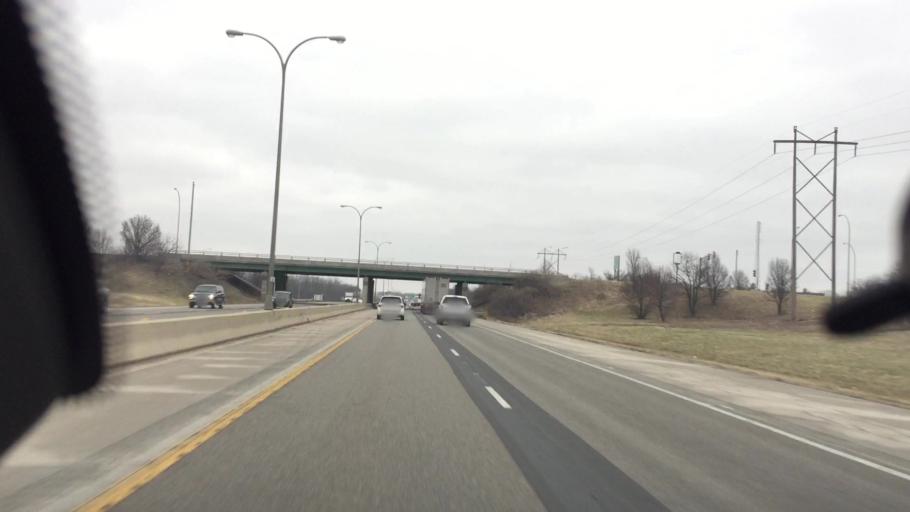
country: US
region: Illinois
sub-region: Champaign County
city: Urbana
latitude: 40.1346
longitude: -88.2214
